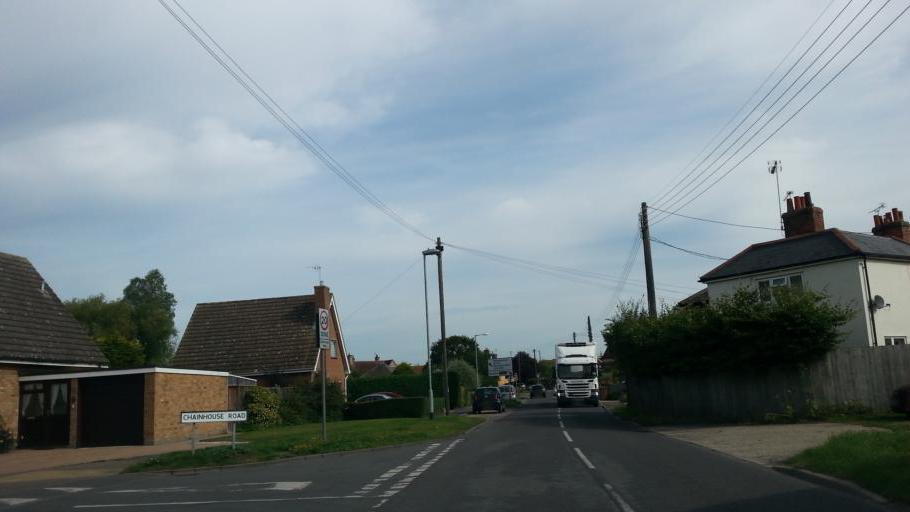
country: GB
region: England
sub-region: Suffolk
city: Needham Market
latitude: 52.1498
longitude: 1.0539
